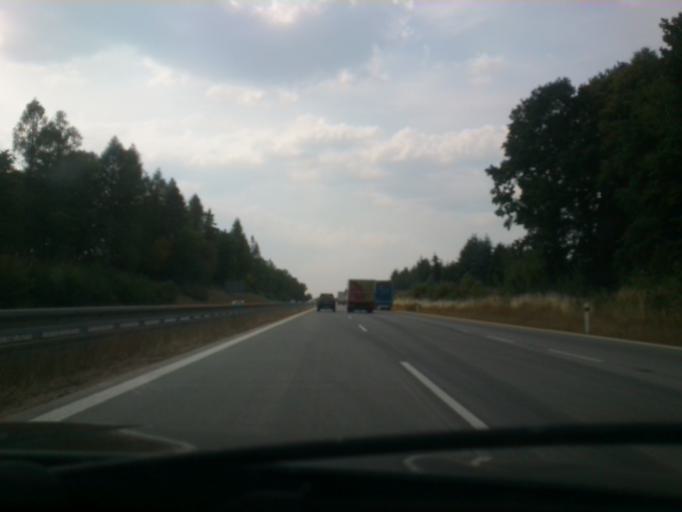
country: CZ
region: Central Bohemia
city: Divisov
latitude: 49.7994
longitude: 14.9136
